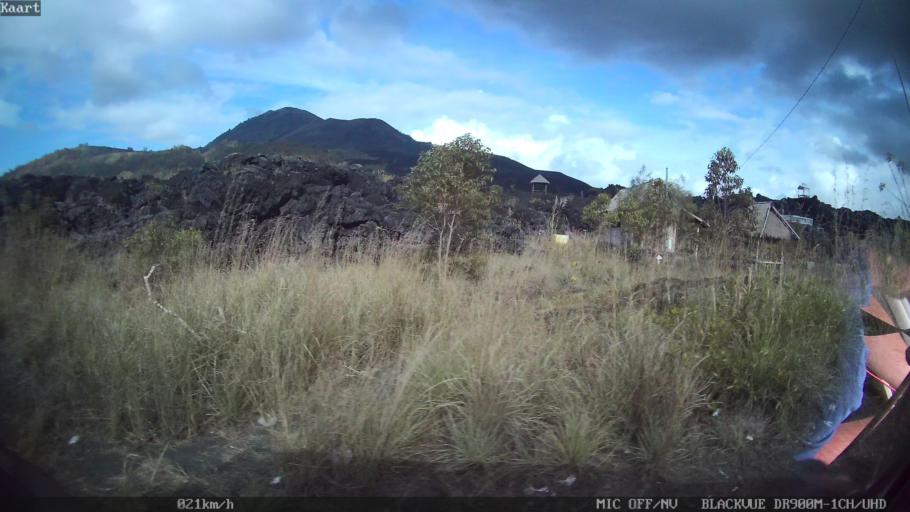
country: ID
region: Bali
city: Banjar Kedisan
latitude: -8.2400
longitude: 115.3525
